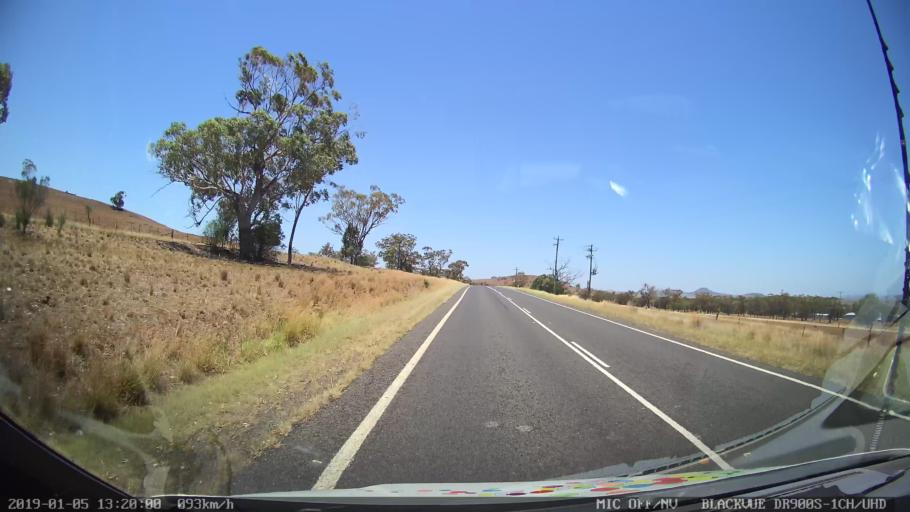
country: AU
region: New South Wales
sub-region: Gunnedah
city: Gunnedah
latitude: -31.1004
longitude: 149.9287
